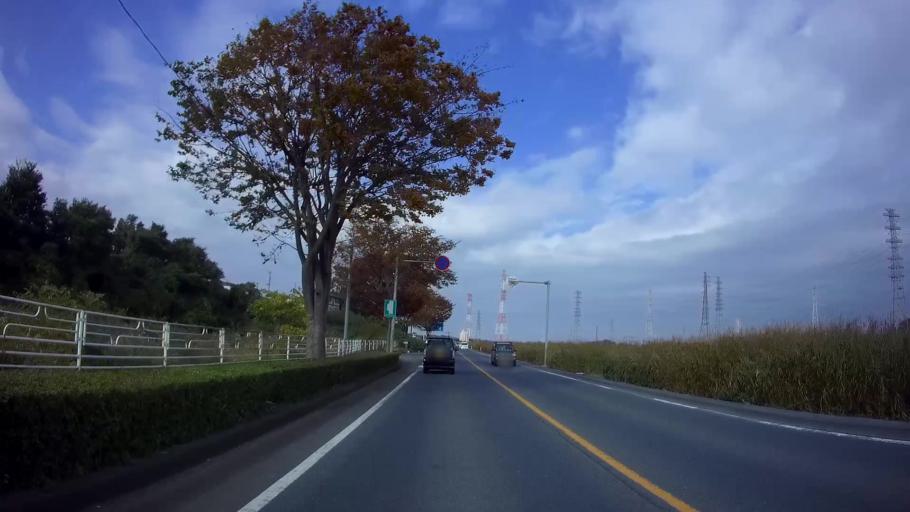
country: JP
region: Saitama
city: Honjo
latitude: 36.2217
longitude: 139.2332
